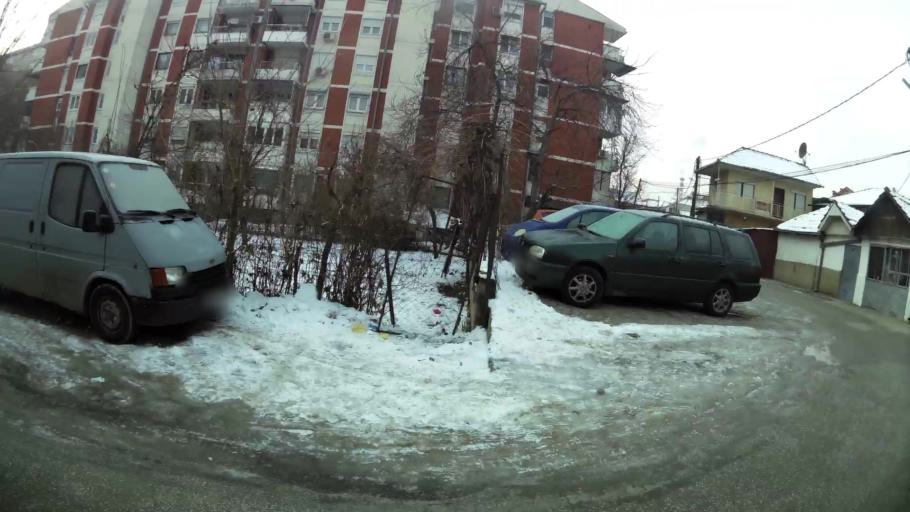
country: MK
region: Cair
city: Cair
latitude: 42.0181
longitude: 21.4393
